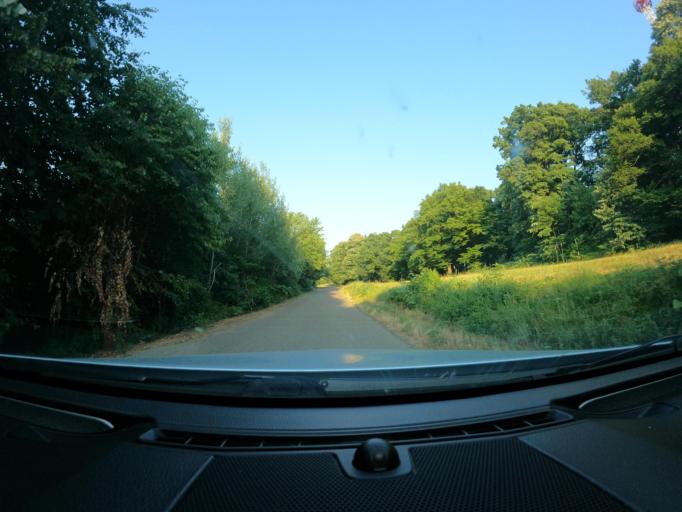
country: RS
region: Autonomna Pokrajina Vojvodina
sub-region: Juznobacki Okrug
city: Beocin
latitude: 45.1564
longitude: 19.7447
